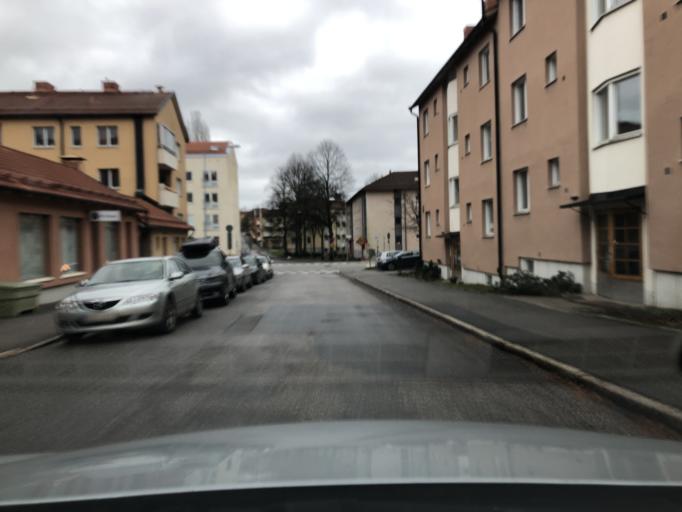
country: SE
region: Stockholm
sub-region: Stockholms Kommun
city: Arsta
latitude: 59.2981
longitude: 18.0439
